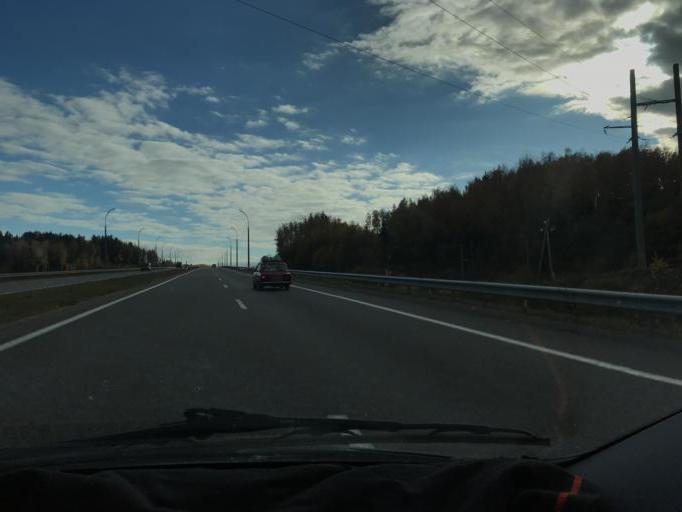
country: BY
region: Minsk
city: Lahoysk
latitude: 54.1827
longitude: 27.8174
